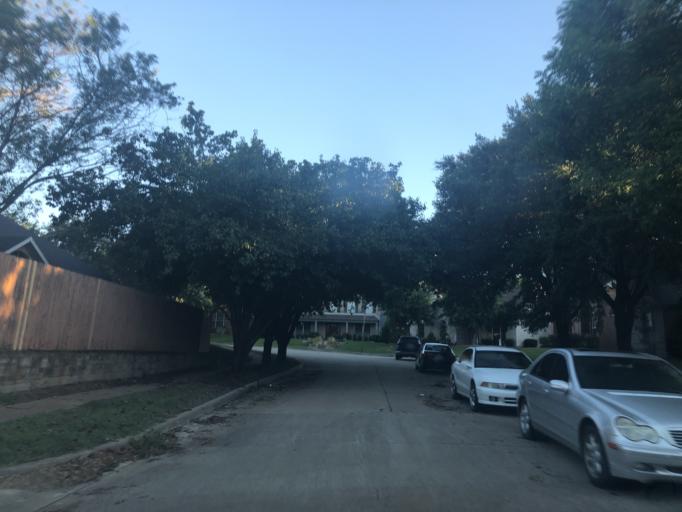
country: US
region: Texas
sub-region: Dallas County
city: Grand Prairie
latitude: 32.6667
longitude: -96.9919
